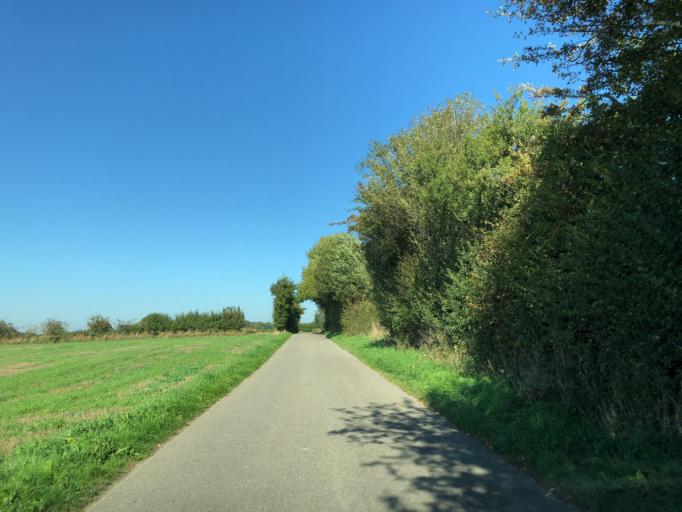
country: DK
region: South Denmark
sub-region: Sonderborg Kommune
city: Dybbol
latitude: 54.9613
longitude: 9.7333
